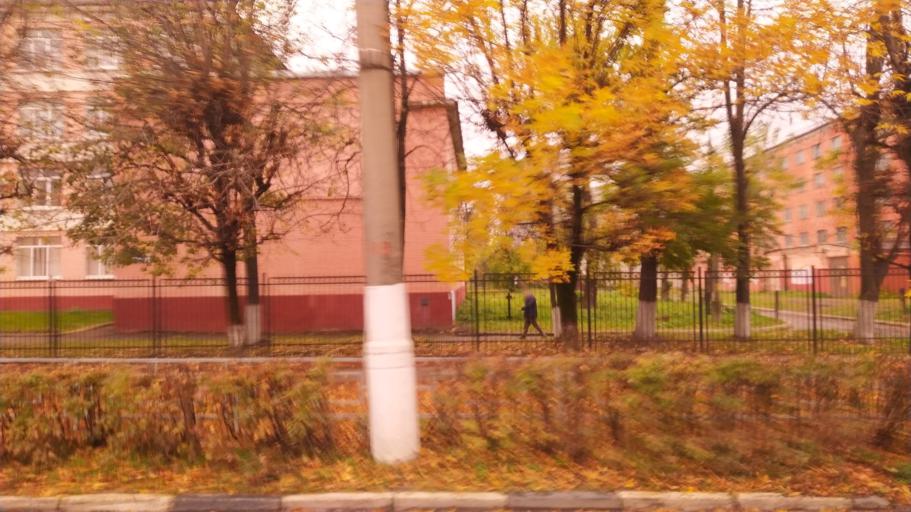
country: RU
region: Tverskaya
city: Tver
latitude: 56.8417
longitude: 35.9256
